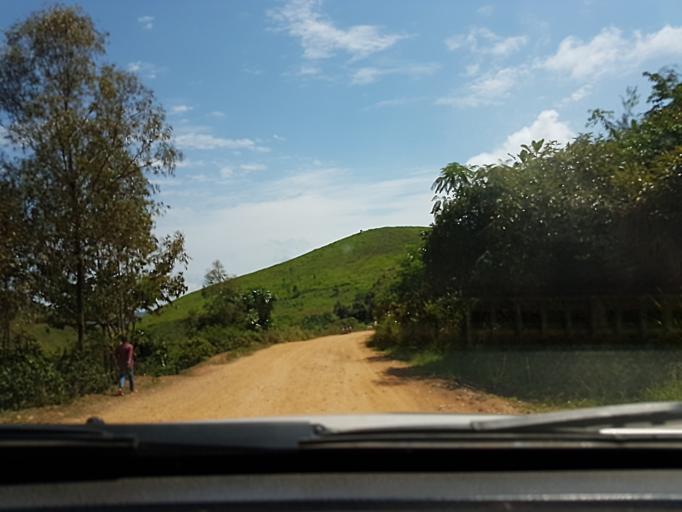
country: RW
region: Western Province
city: Cyangugu
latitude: -2.7015
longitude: 28.9174
